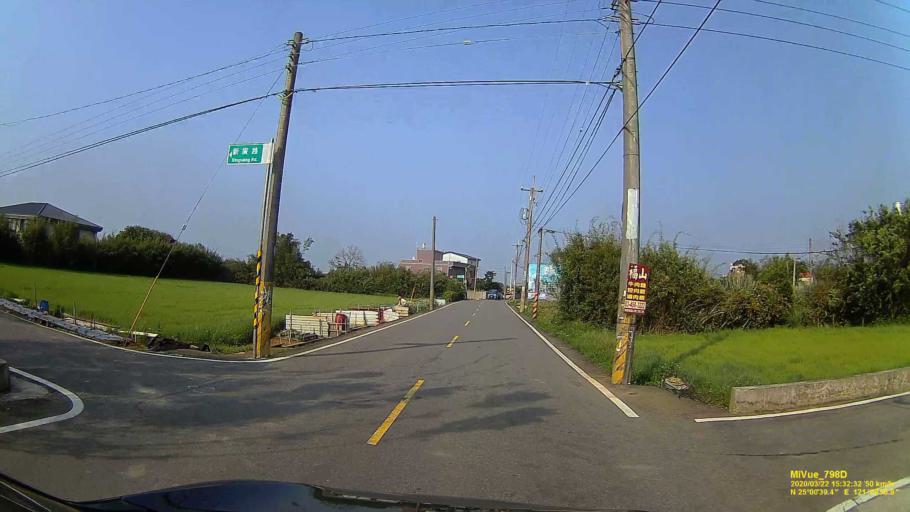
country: TW
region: Taiwan
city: Taoyuan City
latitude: 25.0111
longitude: 121.1499
